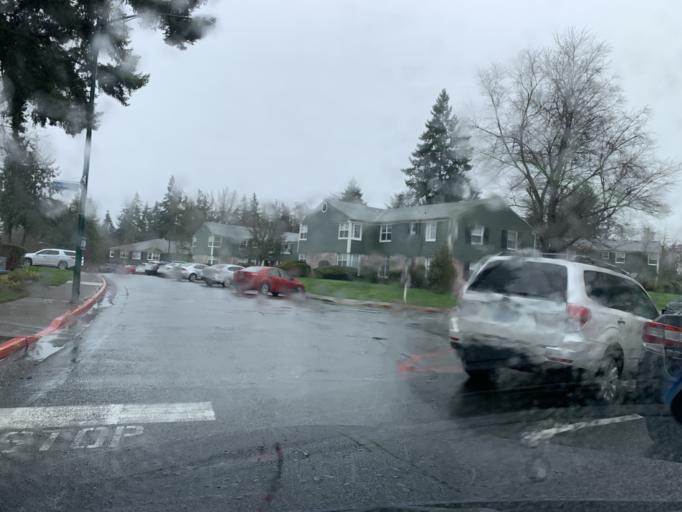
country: US
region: Washington
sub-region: King County
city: Mercer Island
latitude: 47.5793
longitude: -122.2219
